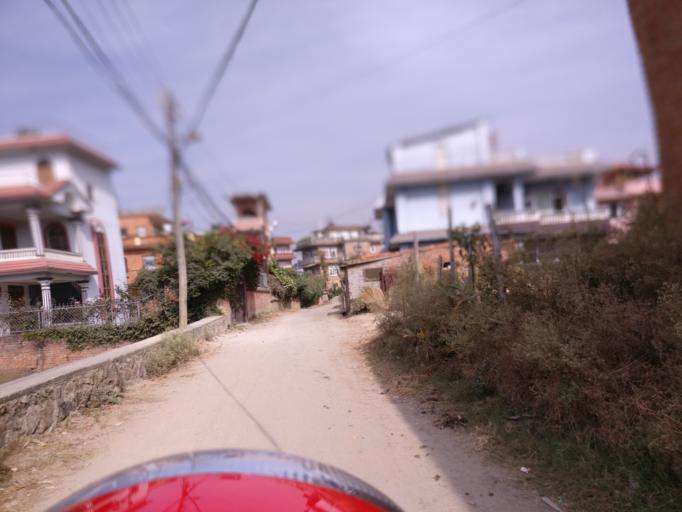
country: NP
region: Central Region
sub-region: Bagmati Zone
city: Patan
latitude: 27.6568
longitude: 85.3127
